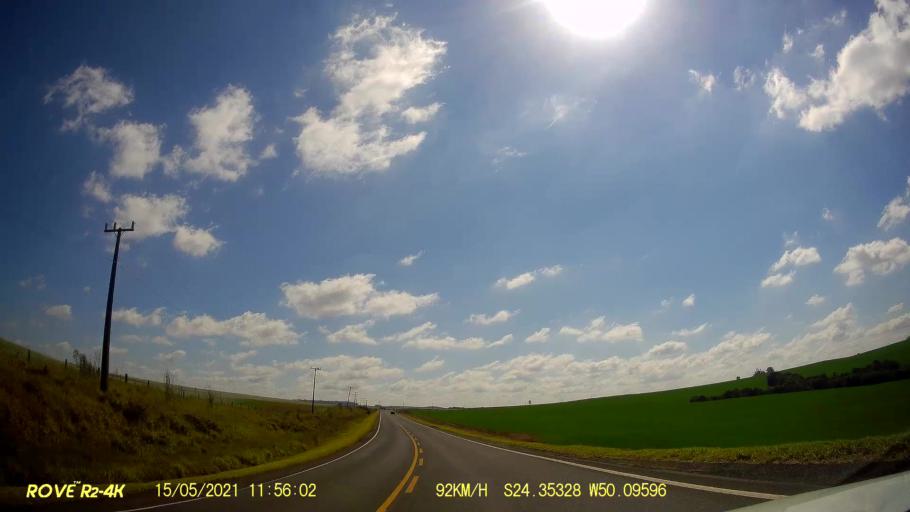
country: BR
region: Parana
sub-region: Pirai Do Sul
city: Pirai do Sul
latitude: -24.3534
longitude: -50.0973
